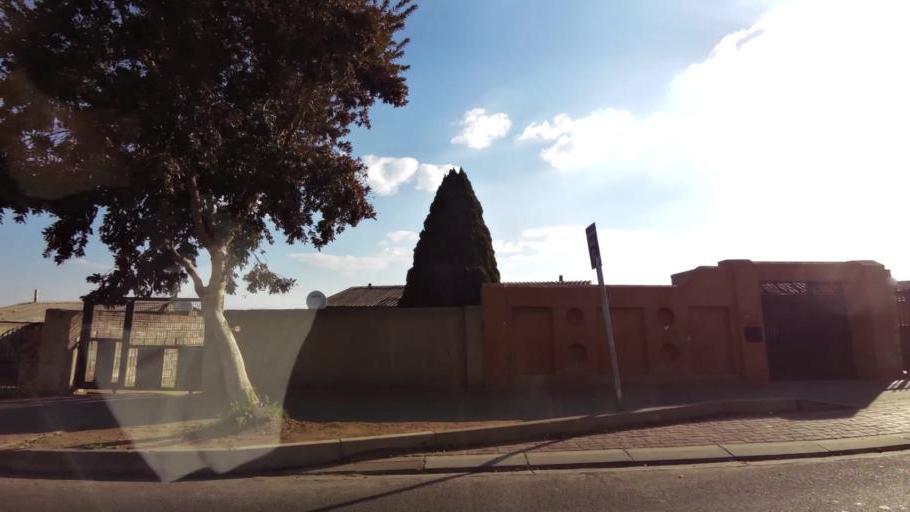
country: ZA
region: Gauteng
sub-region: City of Johannesburg Metropolitan Municipality
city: Roodepoort
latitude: -26.2067
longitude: 27.8841
